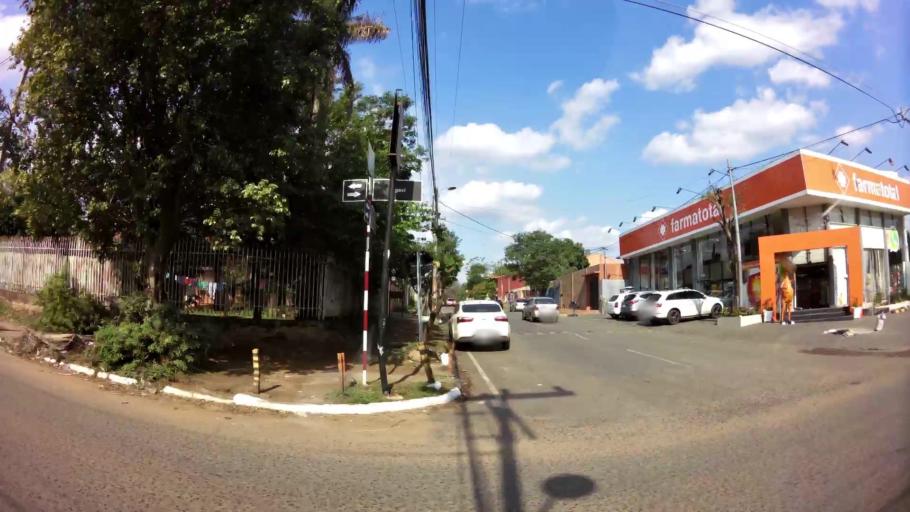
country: PY
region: Central
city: Fernando de la Mora
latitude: -25.3288
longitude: -57.5303
